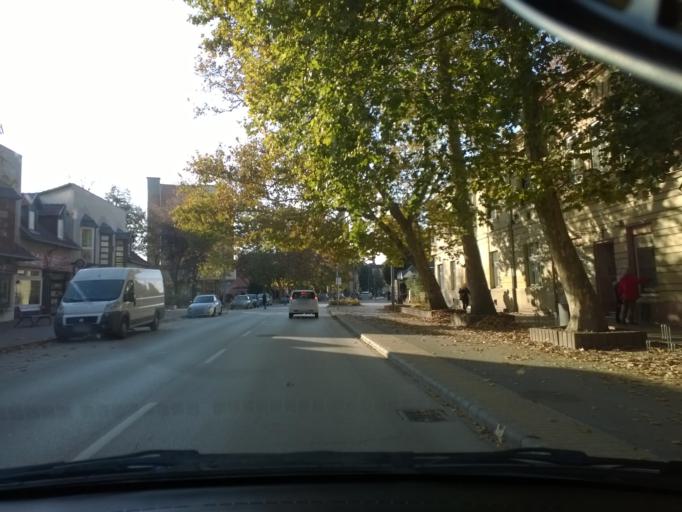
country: HU
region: Csongrad
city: Szentes
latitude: 46.6515
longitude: 20.2624
